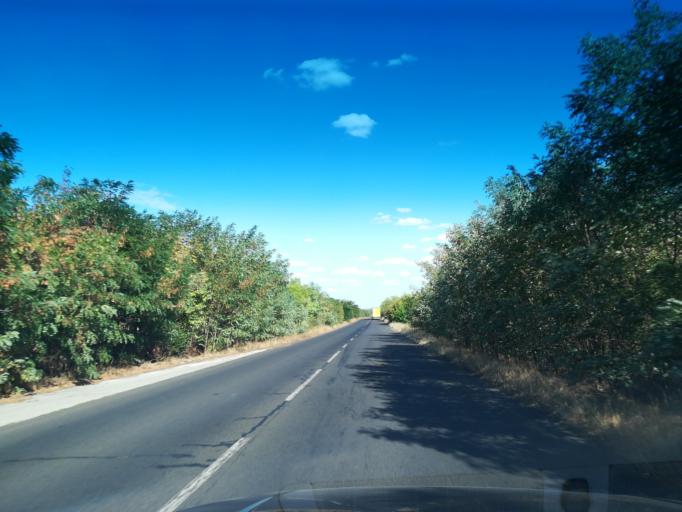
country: BG
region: Stara Zagora
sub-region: Obshtina Chirpan
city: Chirpan
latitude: 42.0562
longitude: 25.2987
